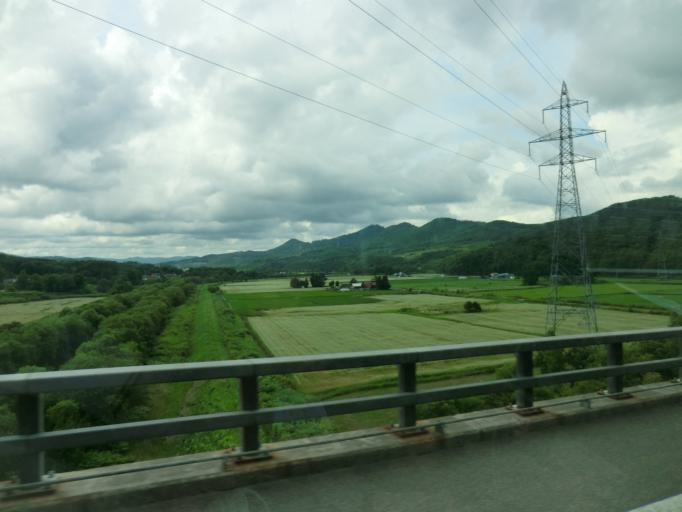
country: JP
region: Hokkaido
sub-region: Asahikawa-shi
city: Asahikawa
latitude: 43.7934
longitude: 142.2809
